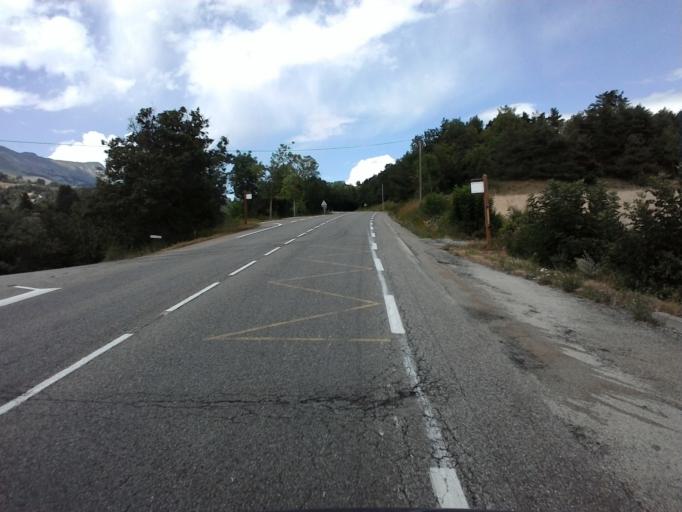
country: FR
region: Provence-Alpes-Cote d'Azur
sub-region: Departement des Hautes-Alpes
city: Gap
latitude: 44.5927
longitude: 6.0808
